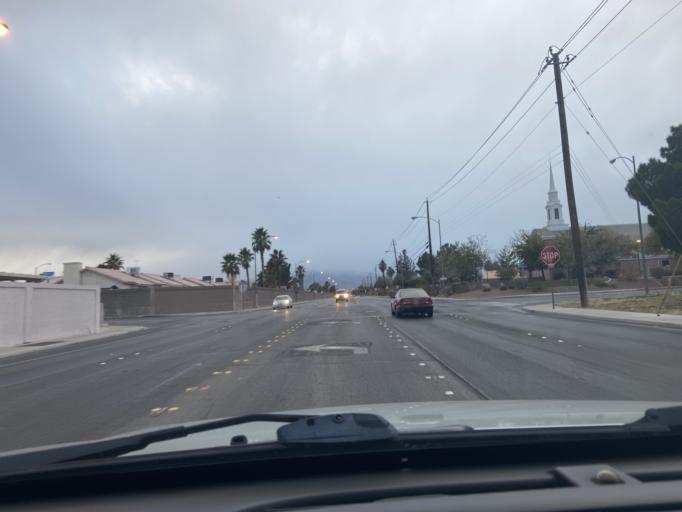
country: US
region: Nevada
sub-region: Clark County
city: Las Vegas
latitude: 36.2320
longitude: -115.1843
